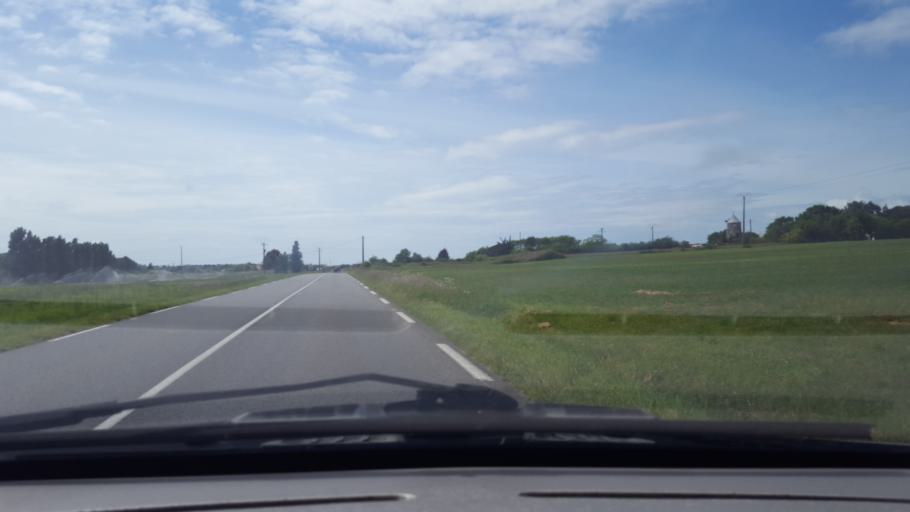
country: FR
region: Pays de la Loire
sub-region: Departement de la Loire-Atlantique
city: Bourgneuf-en-Retz
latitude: 47.0316
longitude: -1.9174
